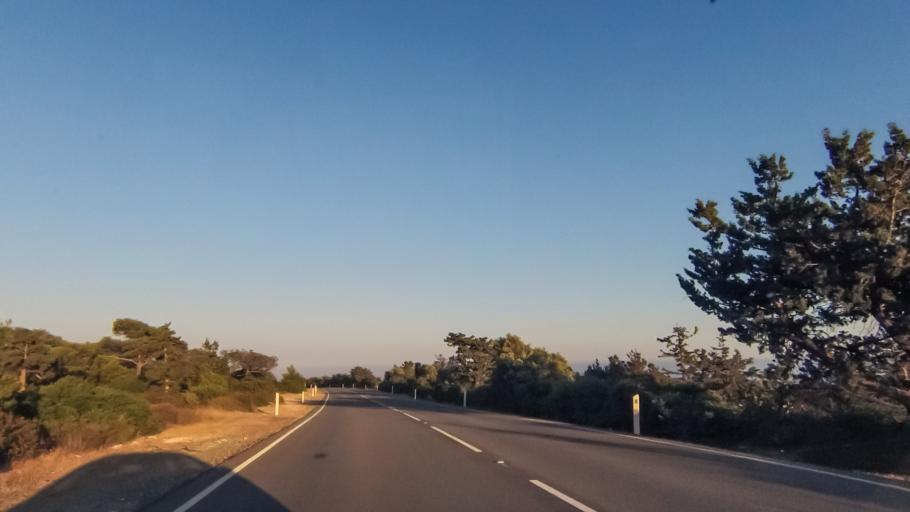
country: CY
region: Limassol
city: Sotira
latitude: 34.6721
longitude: 32.8570
